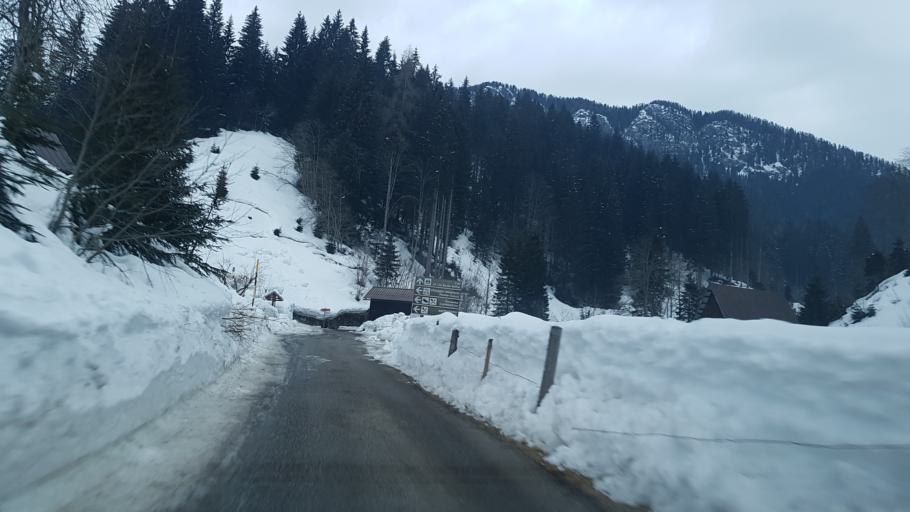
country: IT
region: Friuli Venezia Giulia
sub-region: Provincia di Udine
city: Malborghetto
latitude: 46.5434
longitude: 13.4752
